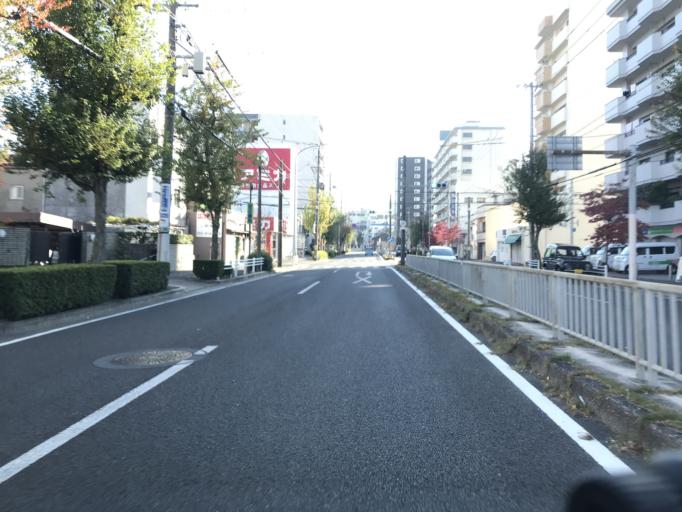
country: JP
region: Aichi
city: Nagoya-shi
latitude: 35.1945
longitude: 136.9298
